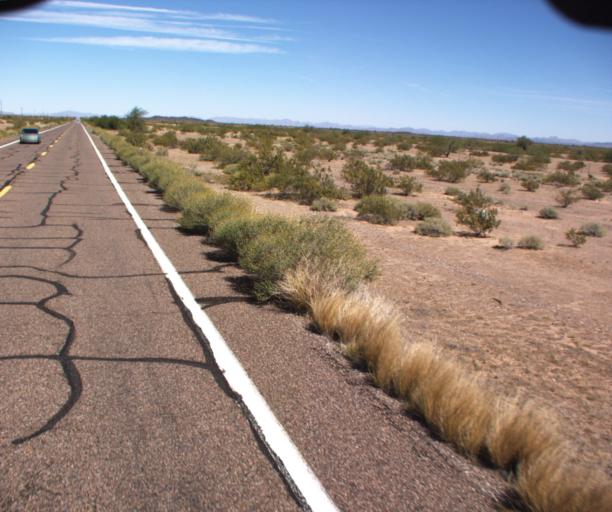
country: US
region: Arizona
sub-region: Maricopa County
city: Gila Bend
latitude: 32.7726
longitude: -112.8148
